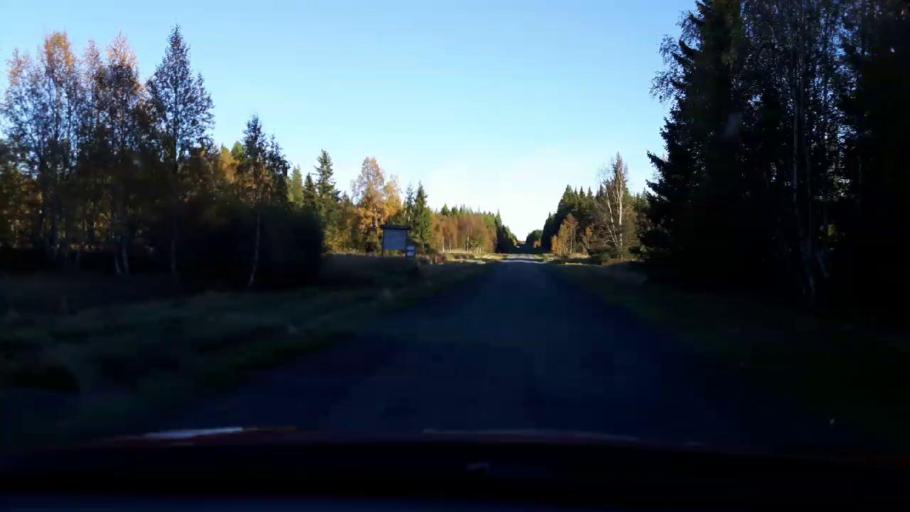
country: SE
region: Jaemtland
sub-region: OEstersunds Kommun
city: Lit
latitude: 63.6030
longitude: 14.8019
